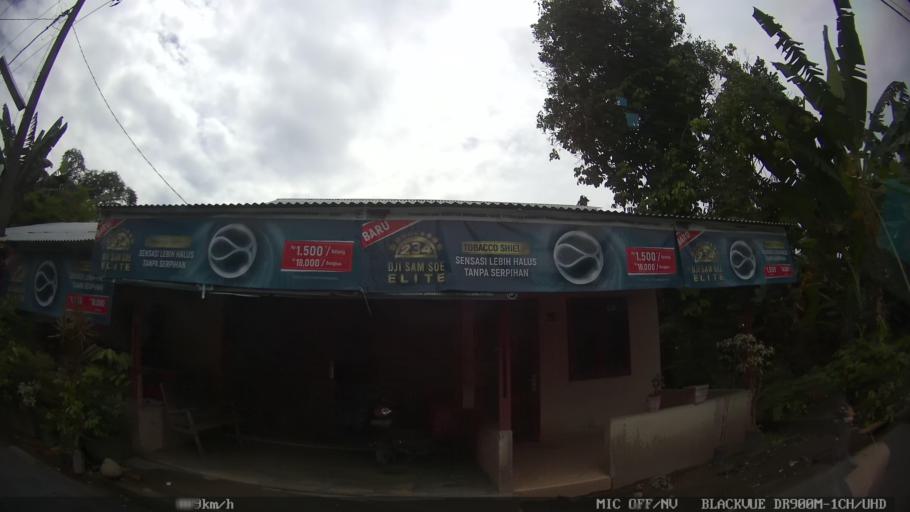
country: ID
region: North Sumatra
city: Sunggal
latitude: 3.6455
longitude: 98.5928
